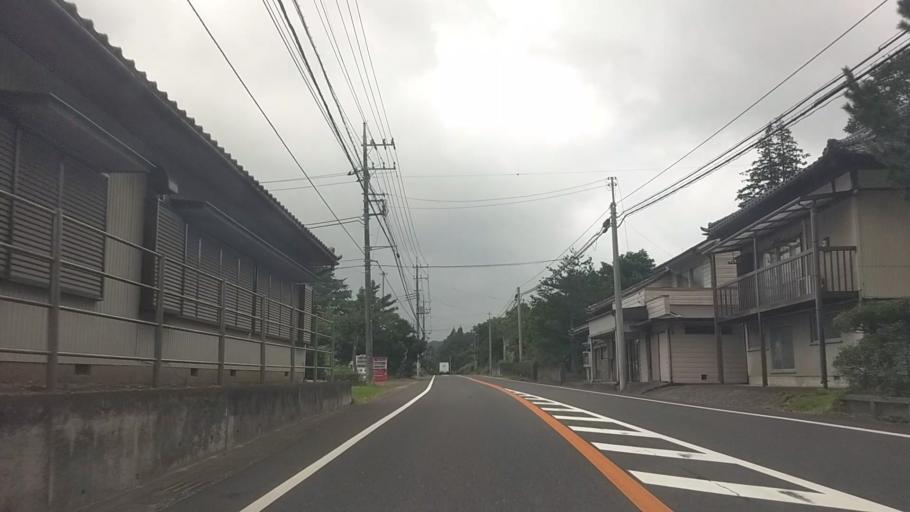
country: JP
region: Chiba
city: Kawaguchi
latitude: 35.2272
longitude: 140.0747
